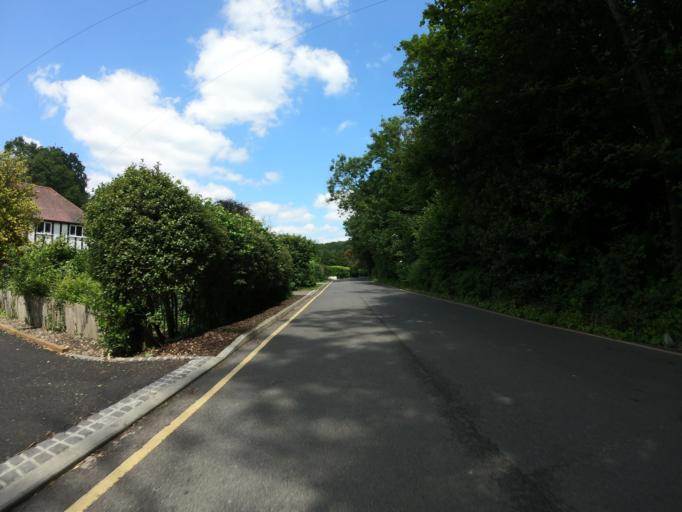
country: GB
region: England
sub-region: Kent
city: Halstead
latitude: 51.3411
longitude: 0.1377
